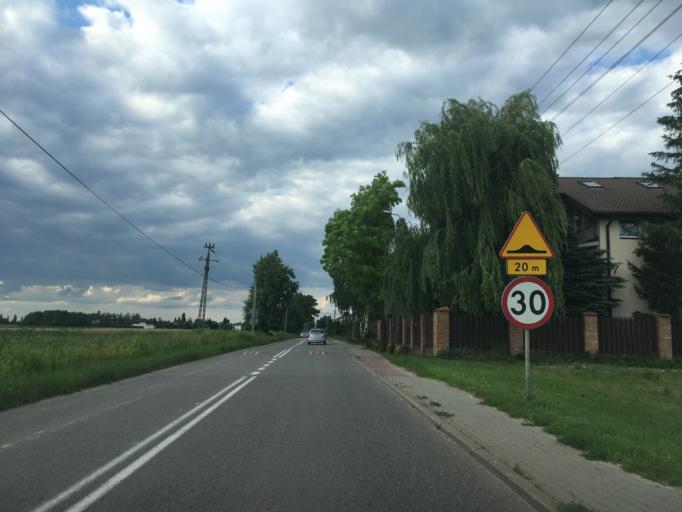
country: PL
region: Masovian Voivodeship
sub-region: Powiat piaseczynski
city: Lesznowola
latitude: 52.0973
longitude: 20.9740
